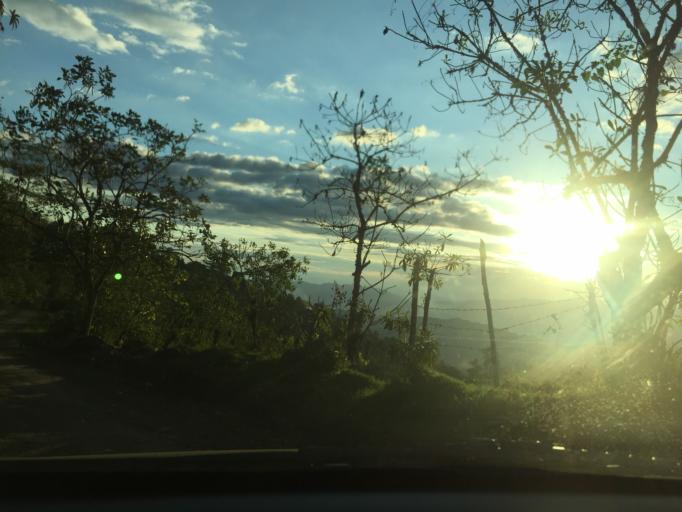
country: CO
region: Cundinamarca
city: Zipacon
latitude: 4.7120
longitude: -74.3971
